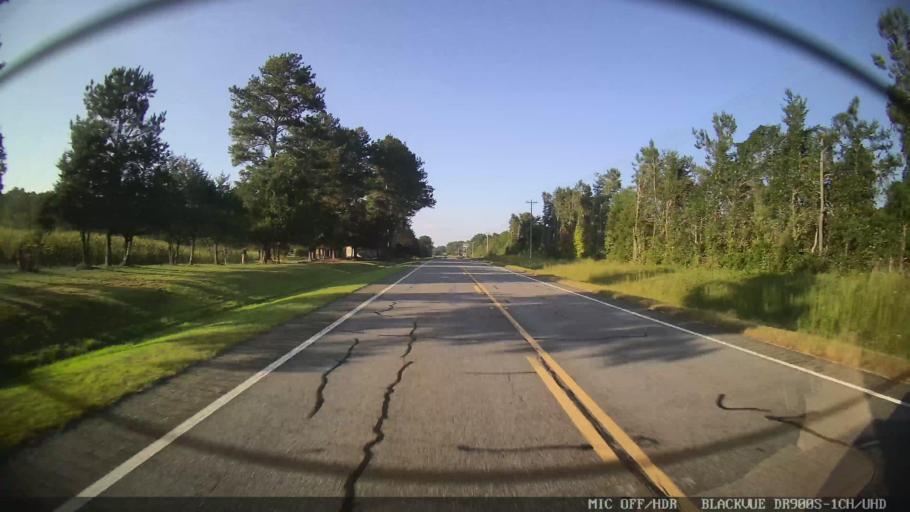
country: US
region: Tennessee
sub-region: Bradley County
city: Wildwood Lake
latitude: 34.9633
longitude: -84.7339
